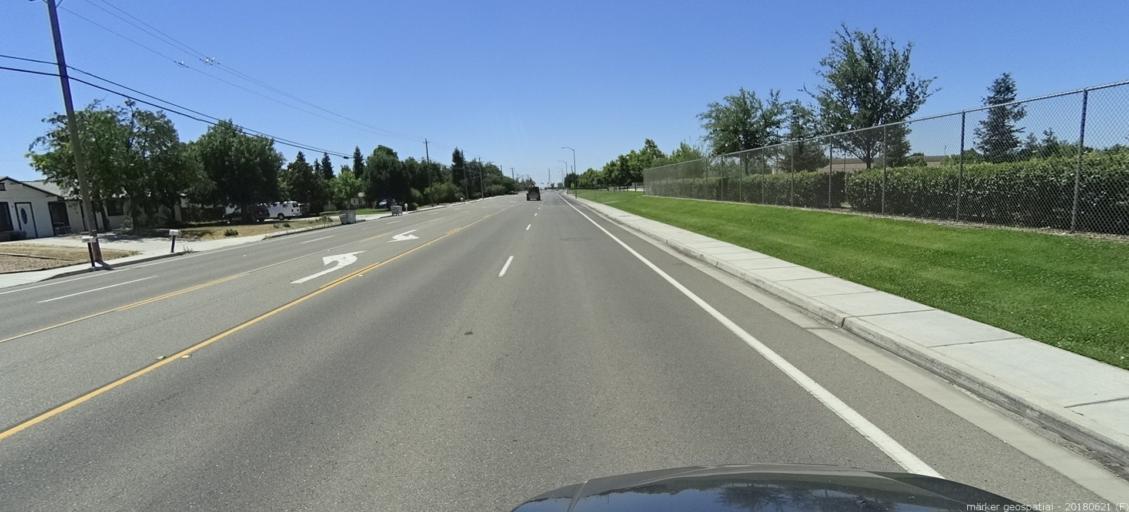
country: US
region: California
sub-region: Madera County
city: Bonadelle Ranchos-Madera Ranchos
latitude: 36.9276
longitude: -119.8943
